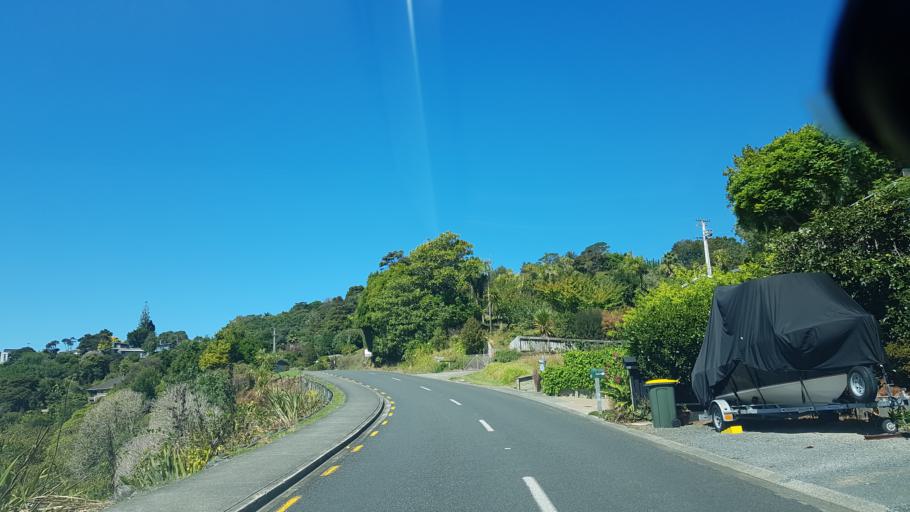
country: NZ
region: Auckland
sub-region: Auckland
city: Warkworth
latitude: -36.3935
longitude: 174.7194
